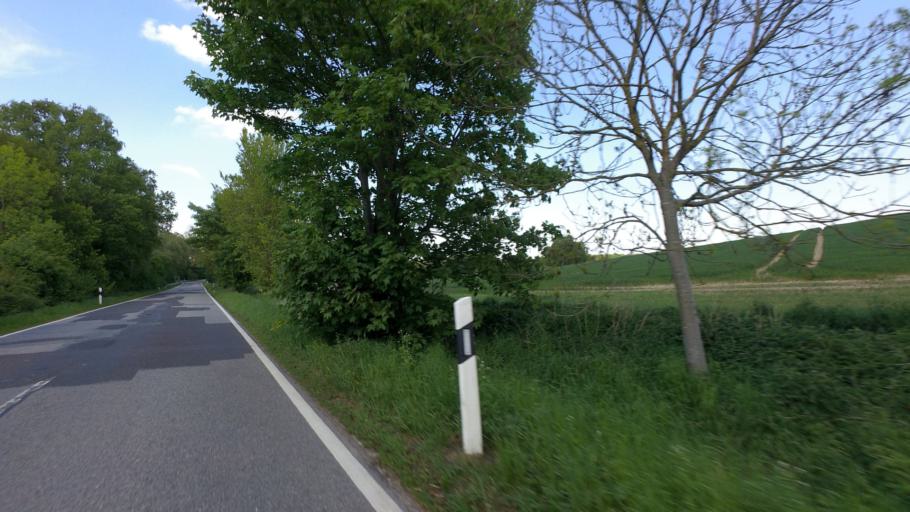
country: DE
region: Mecklenburg-Vorpommern
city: Mollenhagen
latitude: 53.5393
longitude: 12.9296
